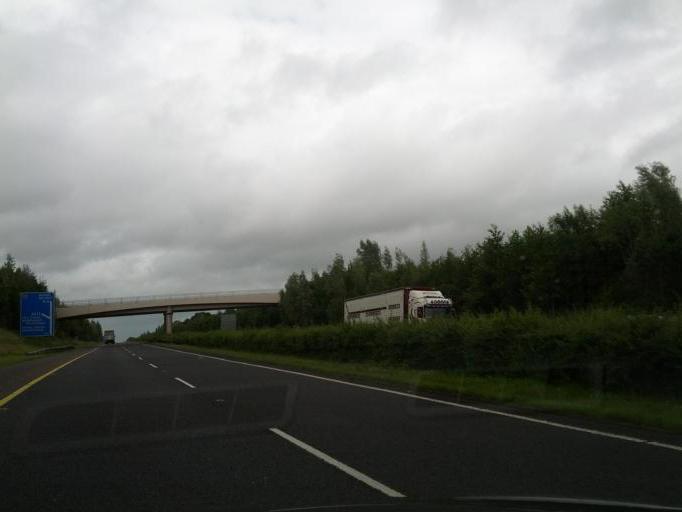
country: IE
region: Munster
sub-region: An Clar
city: Newmarket on Fergus
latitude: 52.7368
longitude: -8.8909
